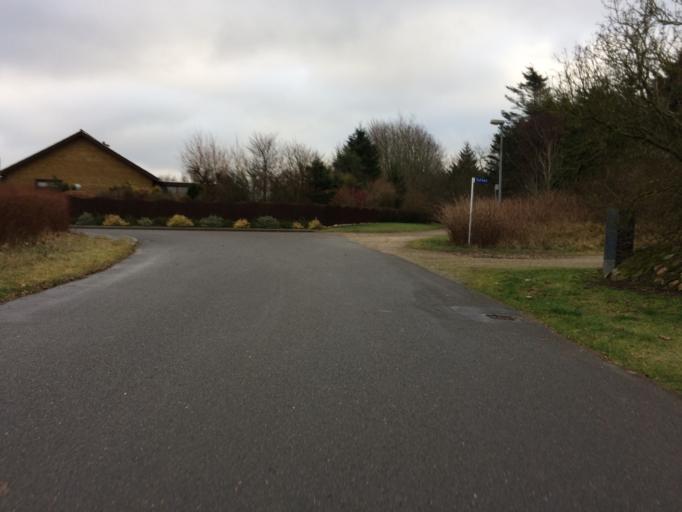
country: DK
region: Central Jutland
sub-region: Holstebro Kommune
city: Ulfborg
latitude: 56.2649
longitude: 8.2455
